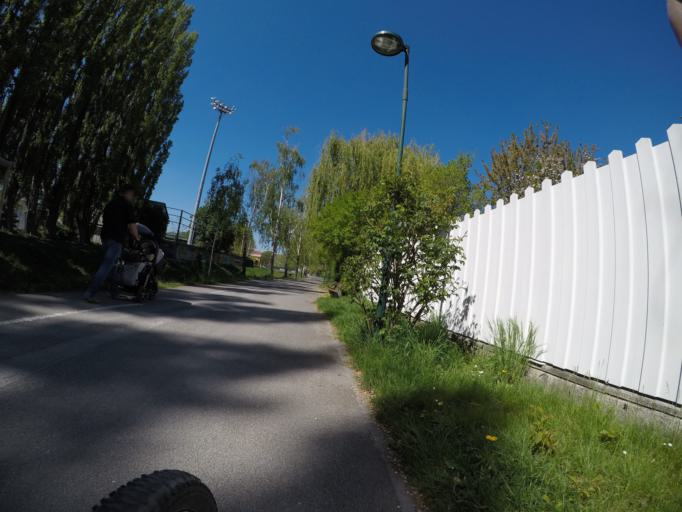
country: AT
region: Lower Austria
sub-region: Politischer Bezirk Modling
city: Wiener Neudorf
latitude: 48.0852
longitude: 16.3030
